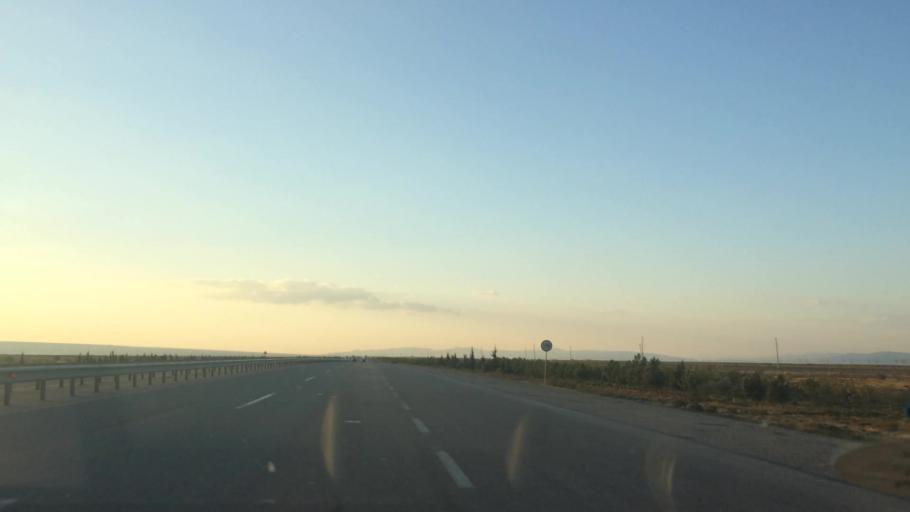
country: AZ
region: Baki
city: Qobustan
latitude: 39.9852
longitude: 49.2106
